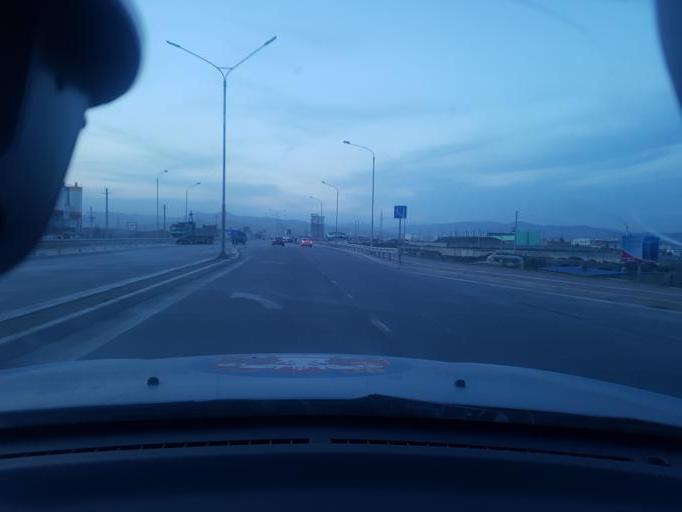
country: MN
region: Ulaanbaatar
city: Ulaanbaatar
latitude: 47.8841
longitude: 106.7852
